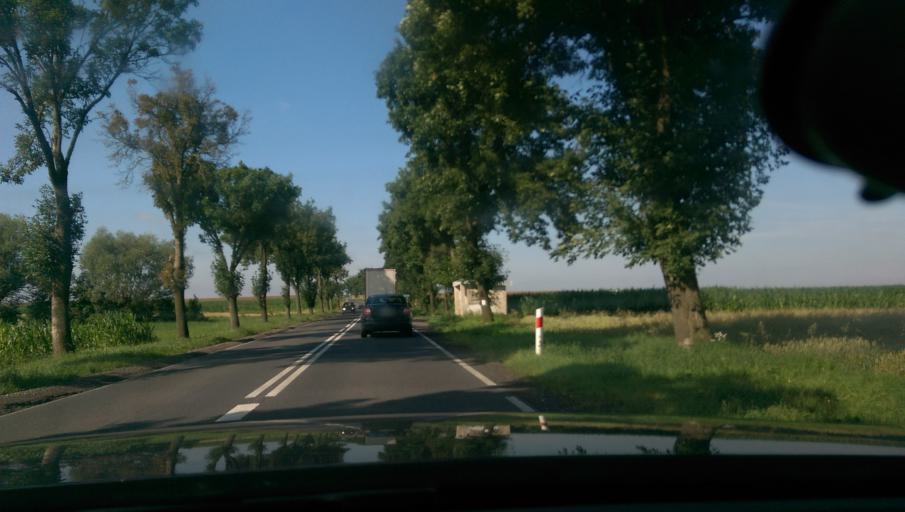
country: PL
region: Masovian Voivodeship
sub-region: Powiat plonski
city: Plonsk
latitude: 52.6416
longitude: 20.4067
